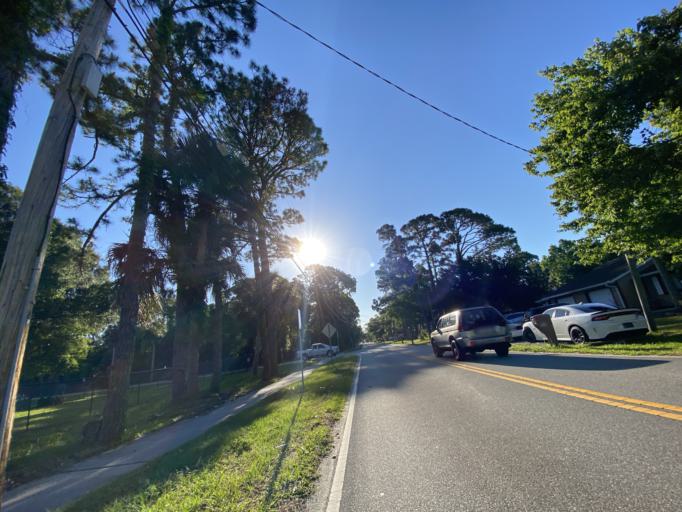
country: US
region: Florida
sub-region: Volusia County
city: Port Orange
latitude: 29.1463
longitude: -81.0004
